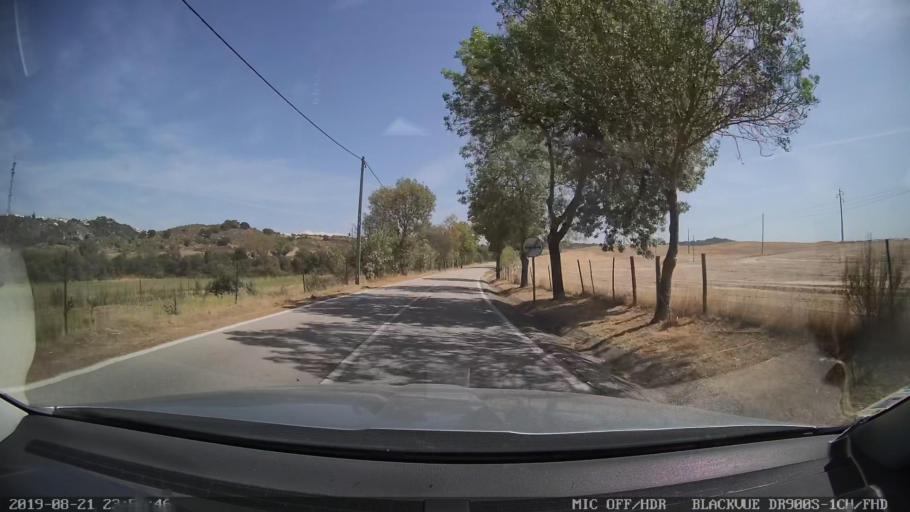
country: PT
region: Castelo Branco
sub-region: Idanha-A-Nova
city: Idanha-a-Nova
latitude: 39.9057
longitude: -7.2332
